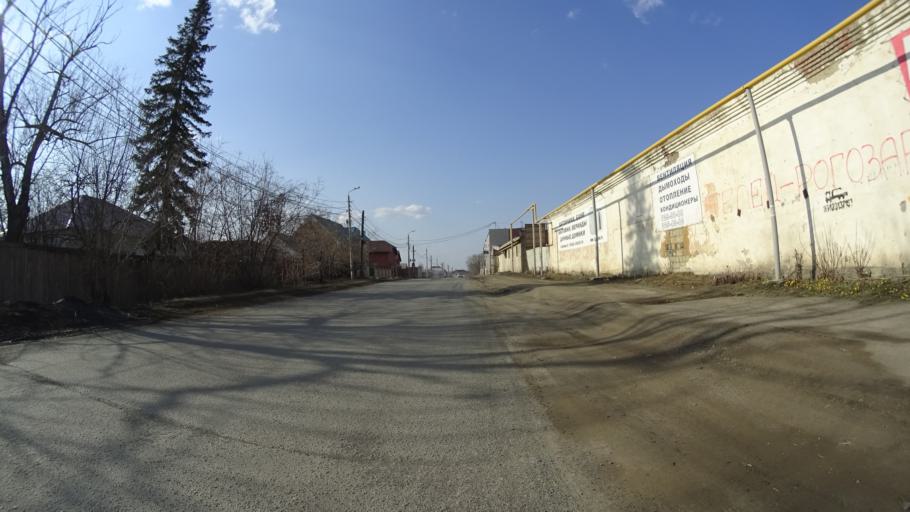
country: RU
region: Chelyabinsk
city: Novosineglazovskiy
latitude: 55.1081
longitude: 61.3348
